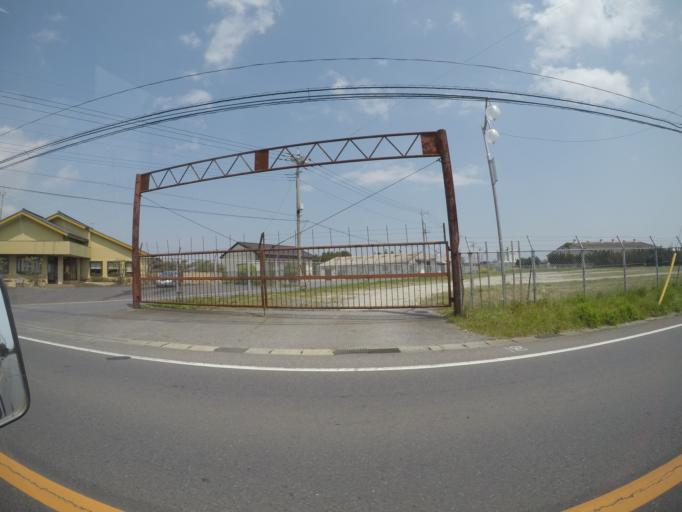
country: JP
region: Chiba
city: Sawara
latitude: 35.8591
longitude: 140.5538
